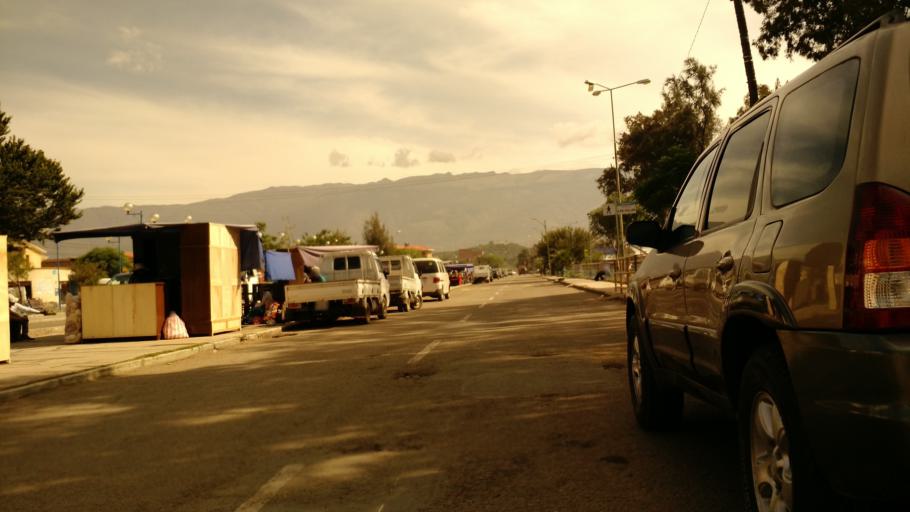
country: BO
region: Cochabamba
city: Cochabamba
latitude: -17.4211
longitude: -66.1601
